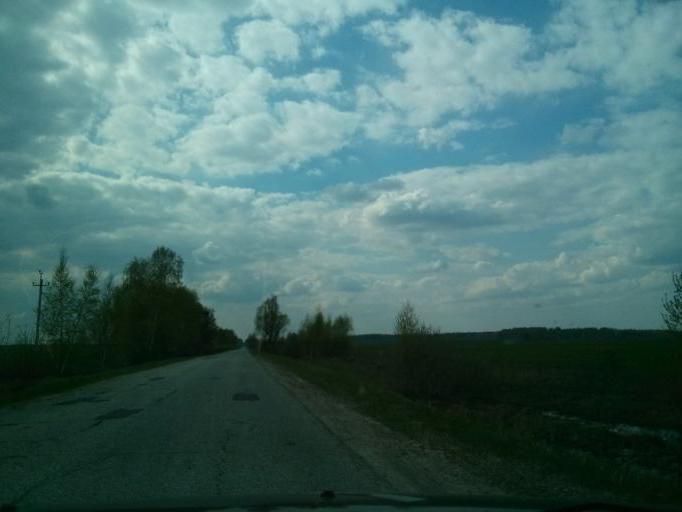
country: RU
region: Nizjnij Novgorod
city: Shimorskoye
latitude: 55.3365
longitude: 41.9040
